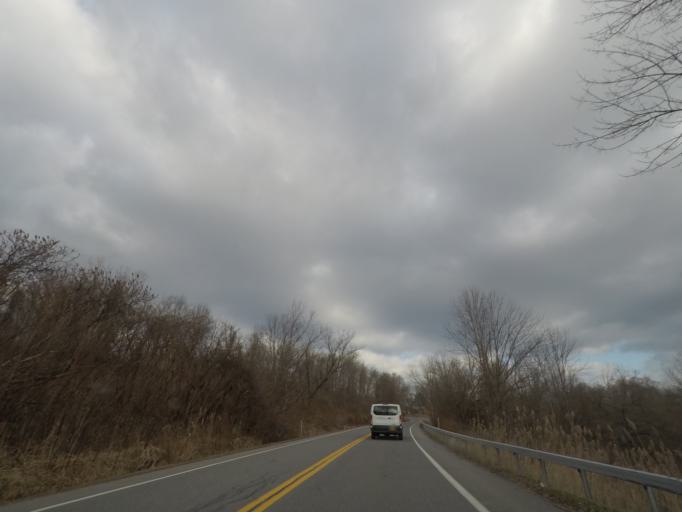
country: US
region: New York
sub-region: Albany County
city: Westmere
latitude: 42.6711
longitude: -73.8791
